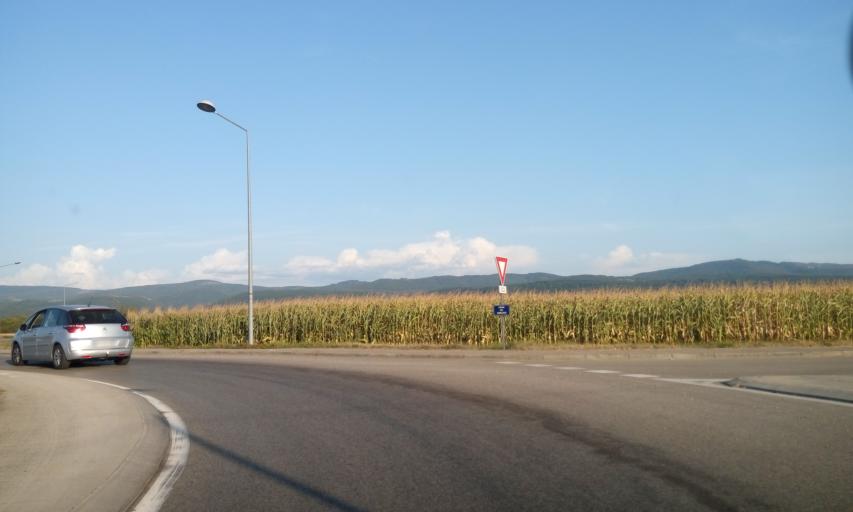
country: FR
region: Rhone-Alpes
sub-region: Departement de l'Ain
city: Ambronay
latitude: 46.0391
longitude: 5.3417
